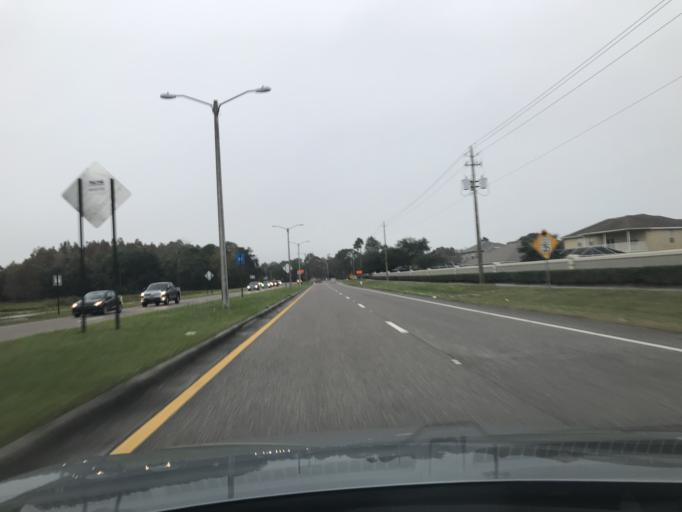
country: US
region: Florida
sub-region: Pinellas County
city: Oldsmar
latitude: 28.0497
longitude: -82.6717
